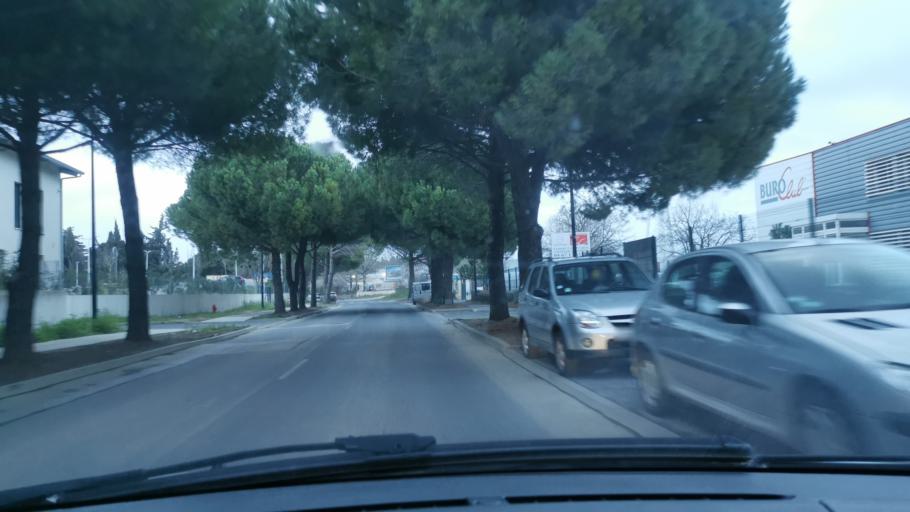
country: FR
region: Languedoc-Roussillon
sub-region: Departement de l'Herault
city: Montpellier
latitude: 43.5821
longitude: 3.8695
